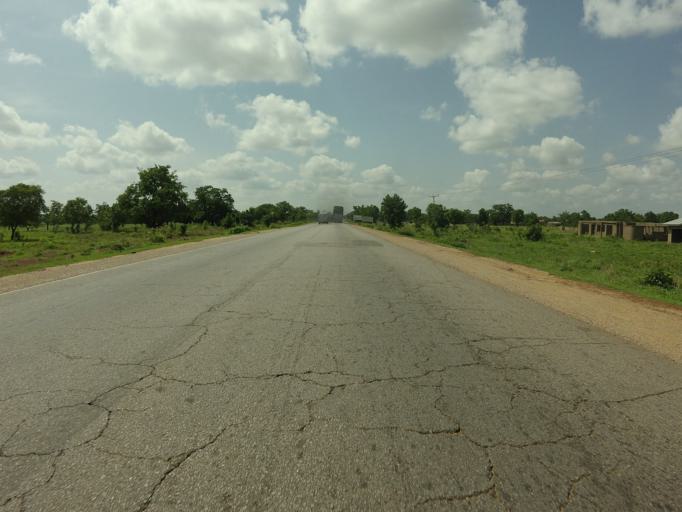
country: GH
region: Northern
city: Savelugu
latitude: 9.5606
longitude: -0.8364
